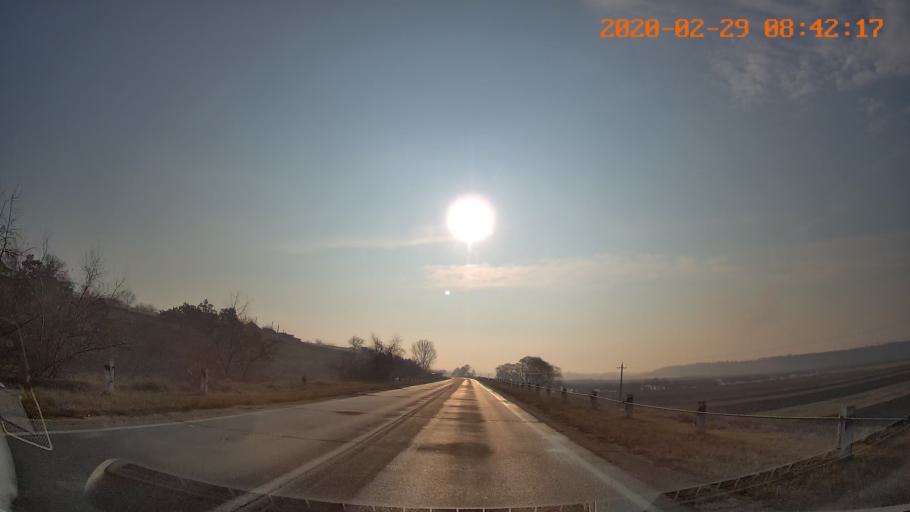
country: MD
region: Anenii Noi
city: Varnita
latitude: 46.9232
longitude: 29.4484
